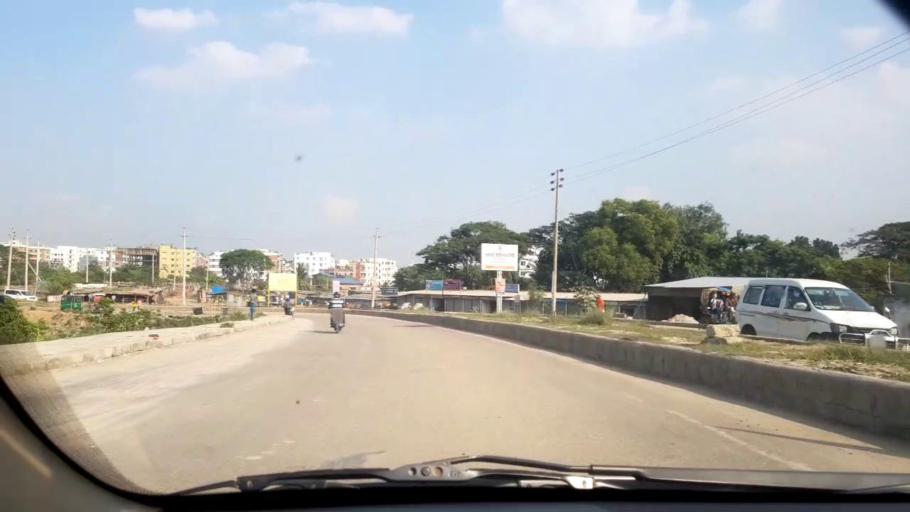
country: BD
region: Dhaka
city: Tungi
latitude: 23.8670
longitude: 90.3750
